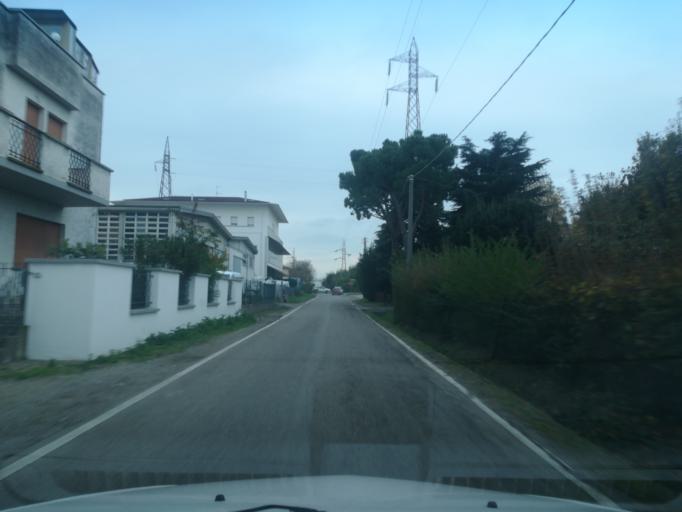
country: IT
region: Emilia-Romagna
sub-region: Provincia di Bologna
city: Imola
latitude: 44.3704
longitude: 11.7117
